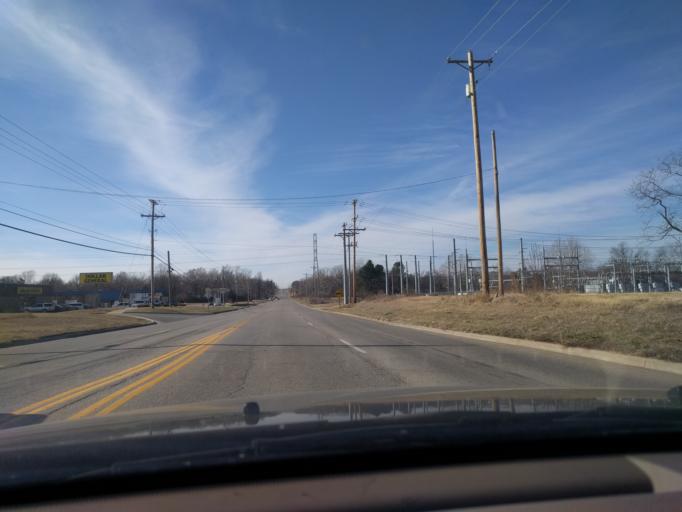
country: US
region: Oklahoma
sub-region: Tulsa County
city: Broken Arrow
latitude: 36.0608
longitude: -95.7096
